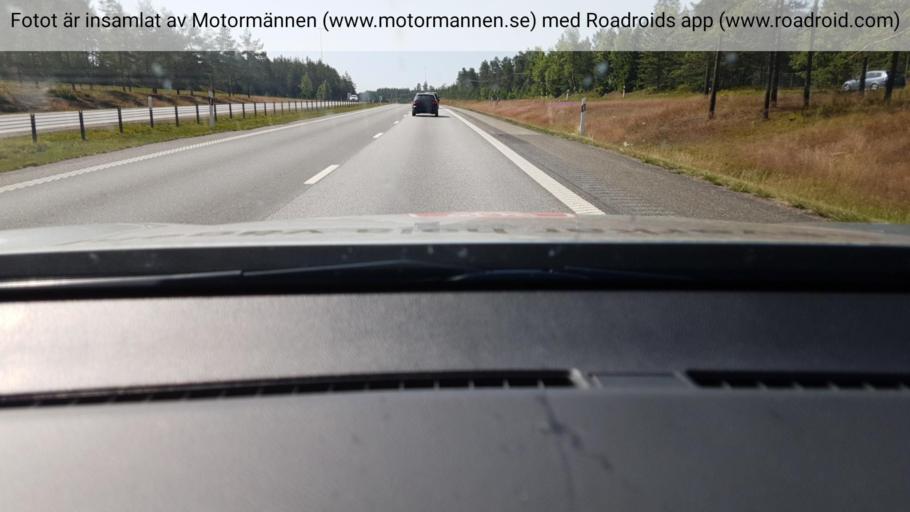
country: SE
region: Joenkoeping
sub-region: Jonkopings Kommun
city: Odensjo
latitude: 57.6869
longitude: 14.1586
